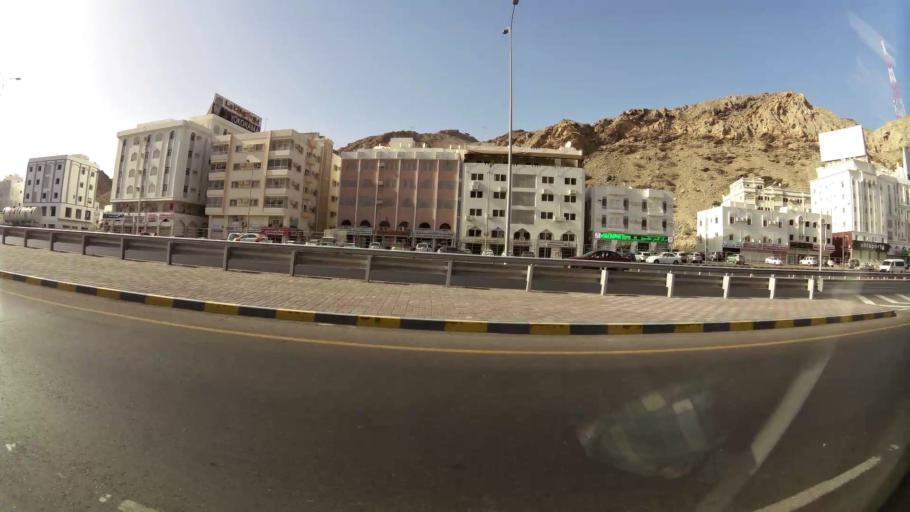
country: OM
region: Muhafazat Masqat
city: Muscat
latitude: 23.5908
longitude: 58.5297
